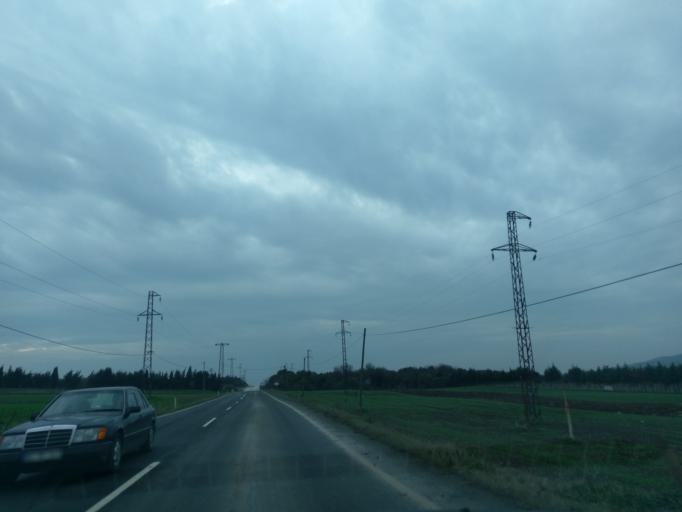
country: TR
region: Istanbul
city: Canta
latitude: 41.1419
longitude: 28.1069
